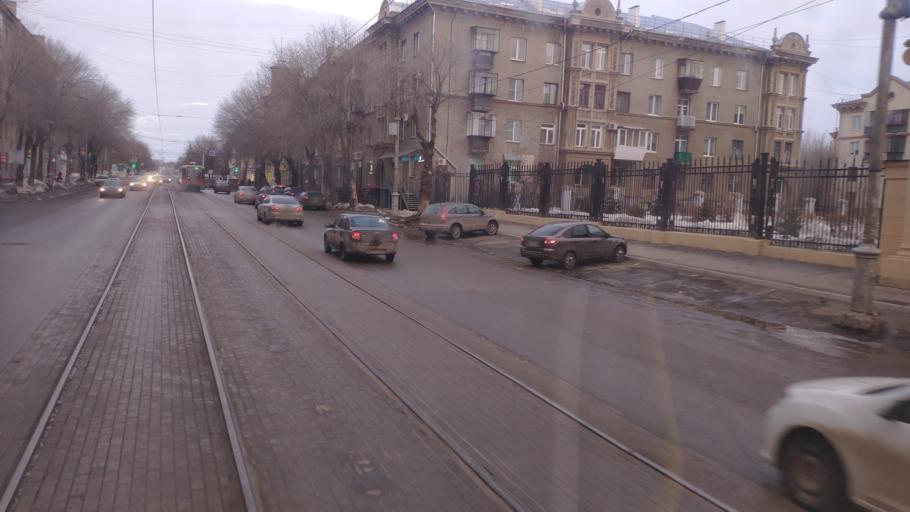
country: RU
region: Chelyabinsk
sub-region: Gorod Magnitogorsk
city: Magnitogorsk
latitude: 53.4178
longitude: 58.9820
